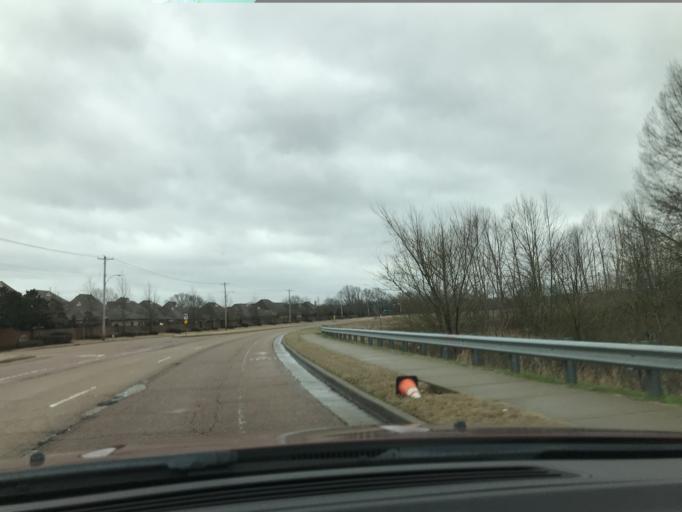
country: US
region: Tennessee
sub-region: Shelby County
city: Collierville
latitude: 35.0844
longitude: -89.6835
